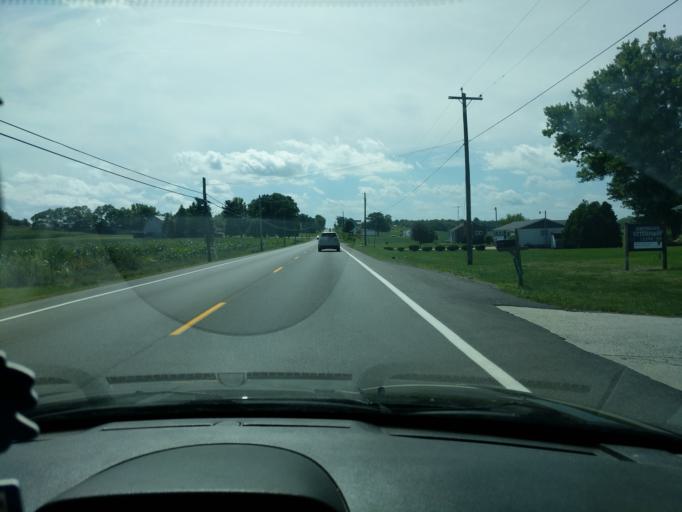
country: US
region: Ohio
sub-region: Logan County
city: Bellefontaine
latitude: 40.3166
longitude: -83.7603
